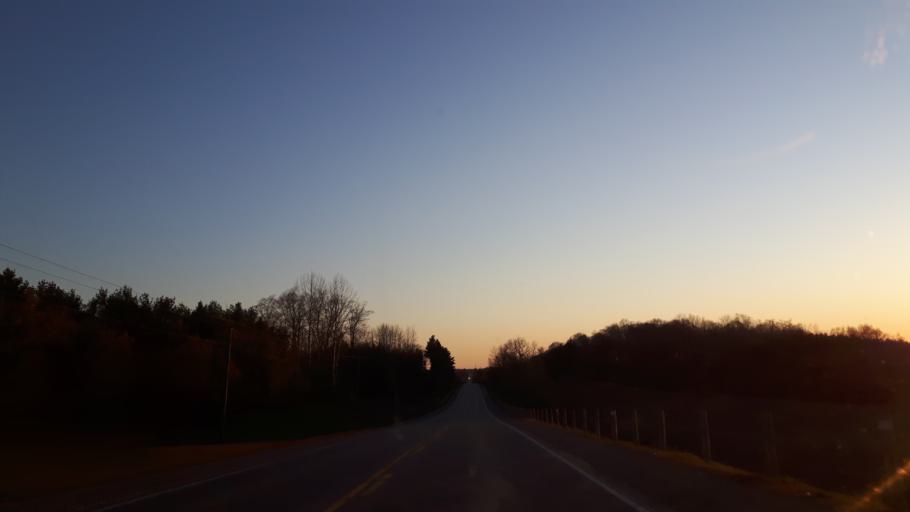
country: CA
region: Ontario
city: Bluewater
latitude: 43.5938
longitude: -81.5667
